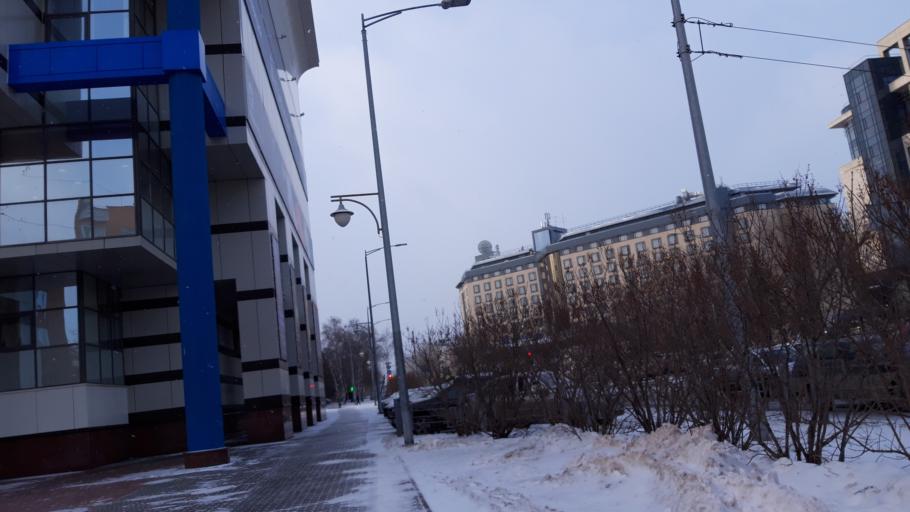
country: RU
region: Tjumen
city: Tyumen
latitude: 57.1544
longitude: 65.5500
